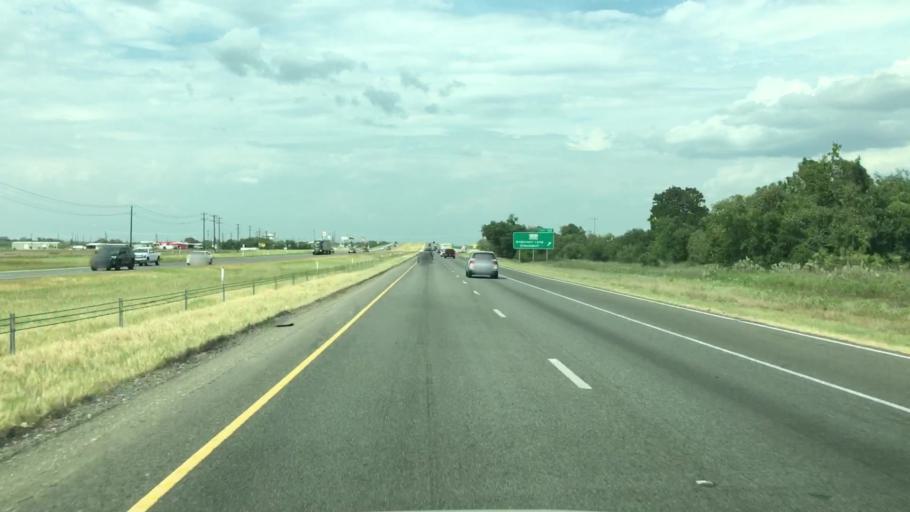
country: US
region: Texas
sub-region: Bexar County
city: Elmendorf
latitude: 29.2097
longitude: -98.4158
